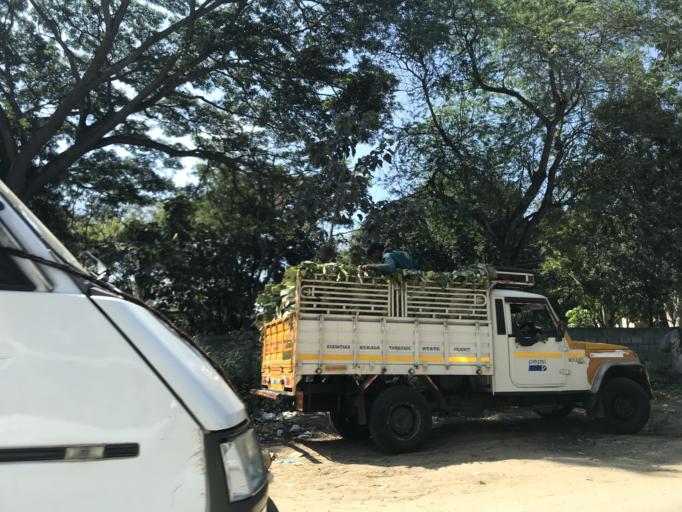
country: IN
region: Karnataka
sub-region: Mysore
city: Heggadadevankote
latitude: 12.0674
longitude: 76.3550
